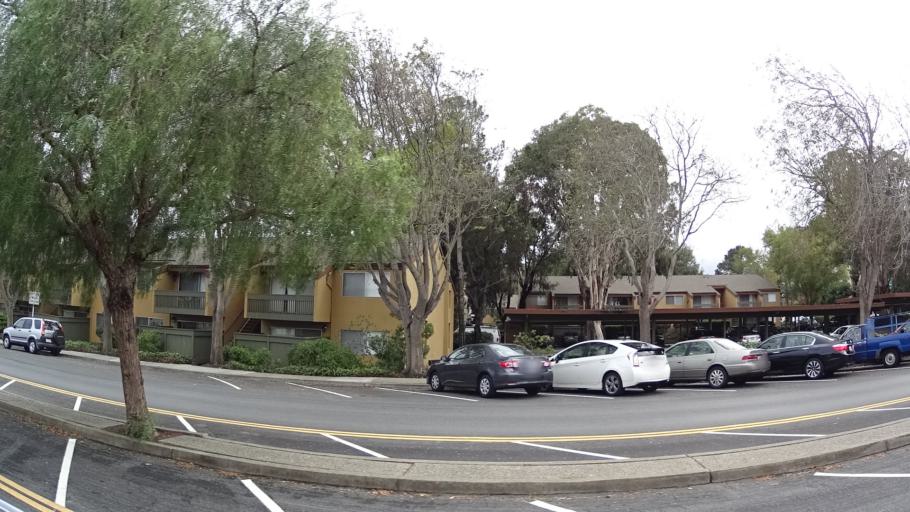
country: US
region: California
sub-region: San Mateo County
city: Millbrae
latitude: 37.6025
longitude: -122.3993
